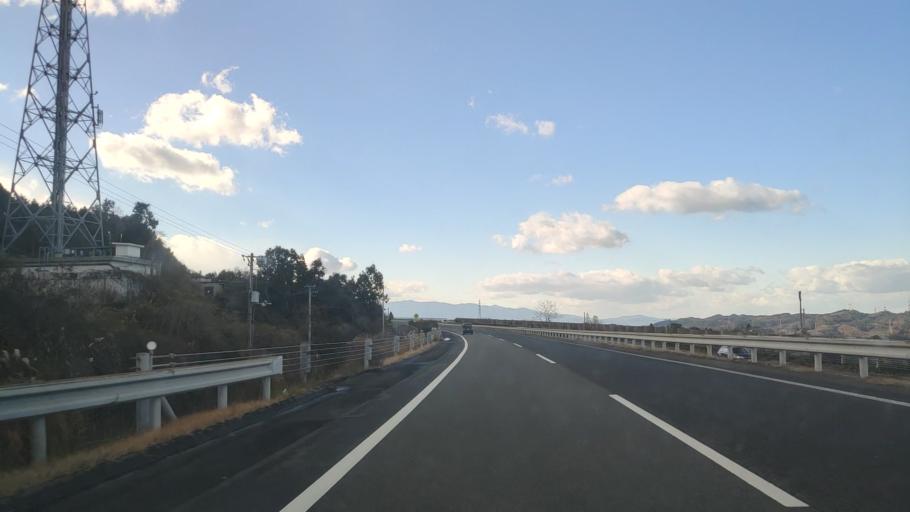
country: JP
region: Ehime
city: Niihama
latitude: 33.9174
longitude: 133.2934
